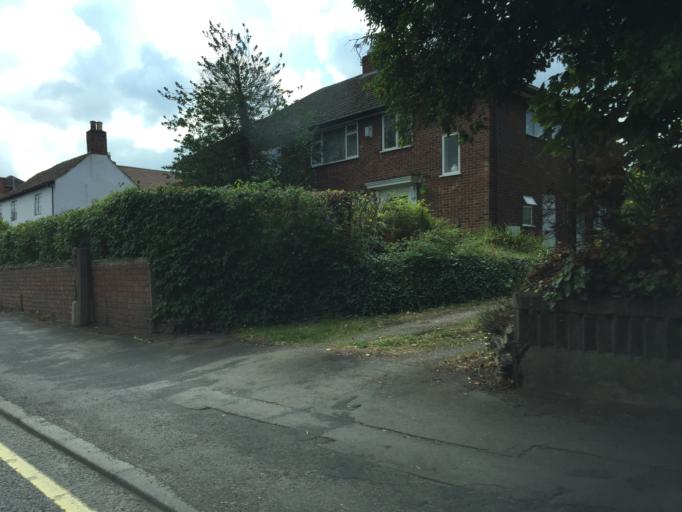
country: GB
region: England
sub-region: Gloucestershire
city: Barnwood
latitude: 51.8661
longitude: -2.2192
